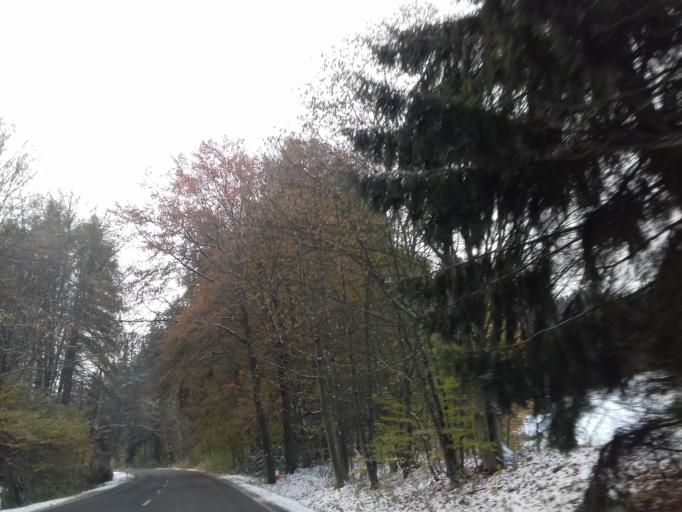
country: CZ
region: Plzensky
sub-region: Okres Domazlice
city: Klenci pod Cerchovem
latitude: 49.4266
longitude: 12.8107
